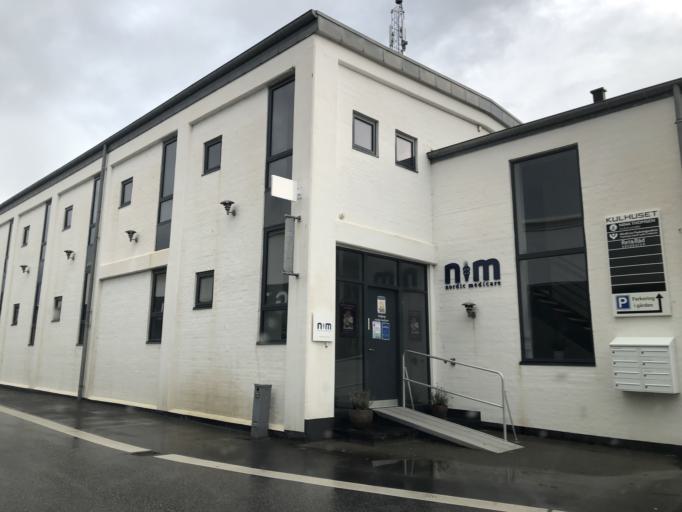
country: DK
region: Central Jutland
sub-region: Lemvig Kommune
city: Lemvig
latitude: 56.5525
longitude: 8.3105
